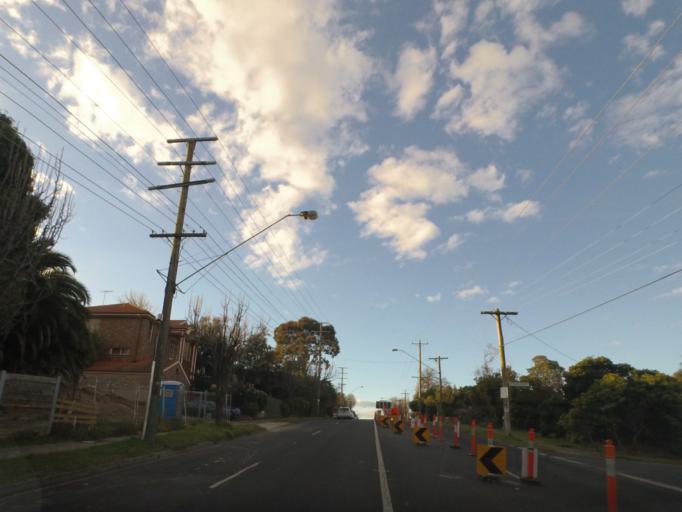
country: AU
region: Victoria
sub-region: Whitehorse
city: Surrey Hills
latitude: -37.8291
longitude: 145.0993
